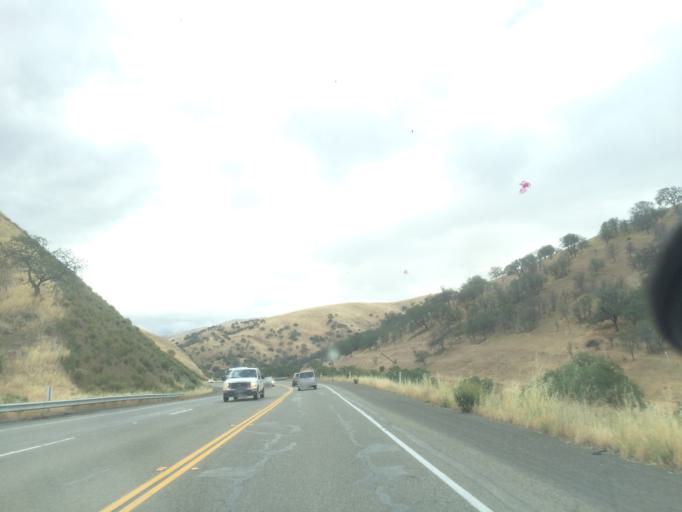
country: US
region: California
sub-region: San Luis Obispo County
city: Shandon
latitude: 35.7819
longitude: -120.1994
